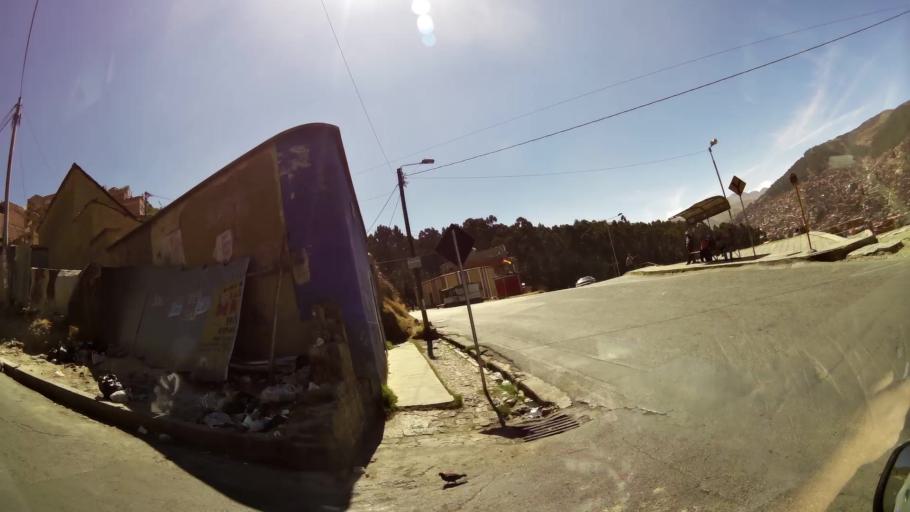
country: BO
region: La Paz
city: La Paz
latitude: -16.4884
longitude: -68.1523
